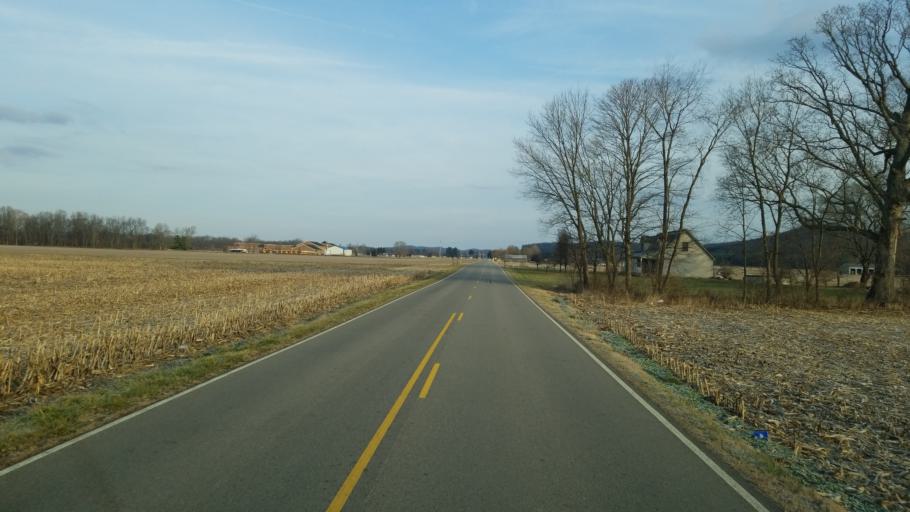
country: US
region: Ohio
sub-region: Ross County
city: Chillicothe
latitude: 39.2736
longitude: -82.8693
